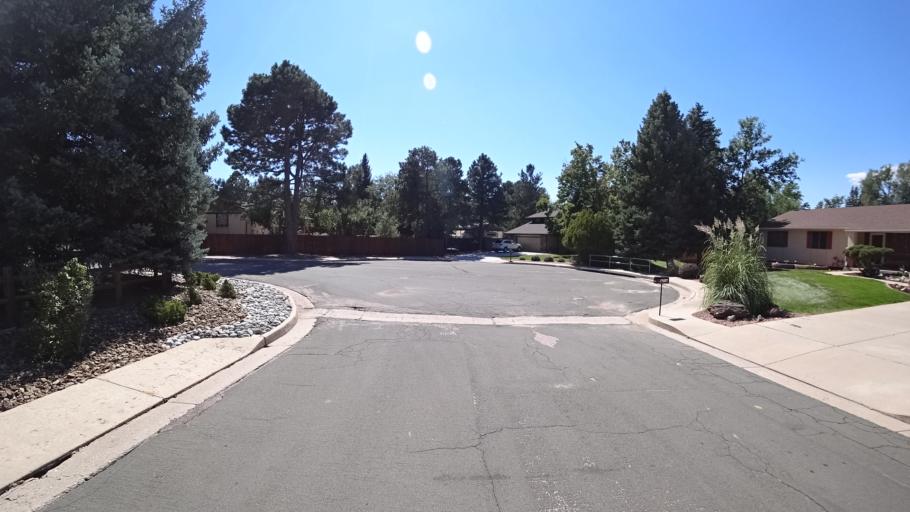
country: US
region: Colorado
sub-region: El Paso County
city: Cimarron Hills
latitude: 38.8667
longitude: -104.7440
